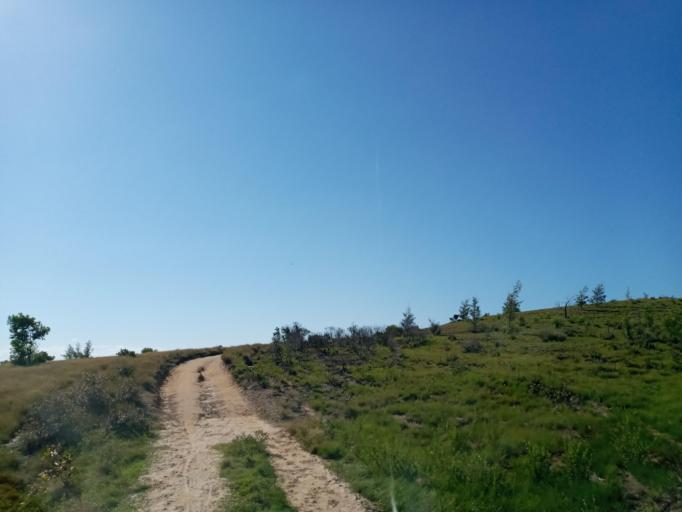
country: MG
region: Anosy
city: Fort Dauphin
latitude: -24.9080
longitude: 47.0909
